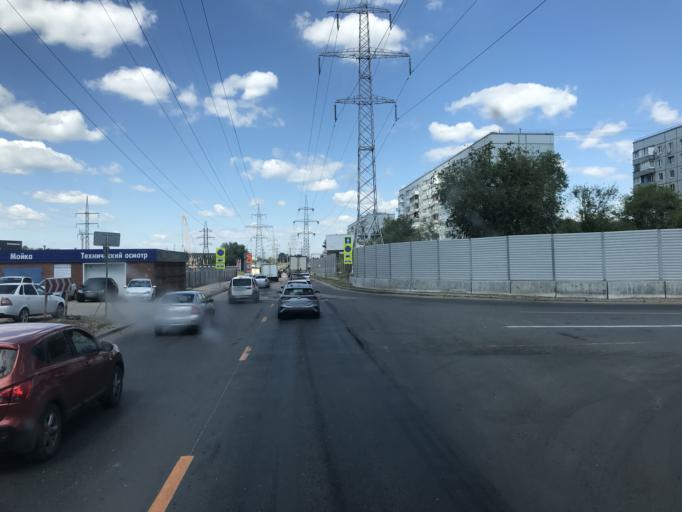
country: RU
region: Samara
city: Zhigulevsk
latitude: 53.4748
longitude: 49.5120
